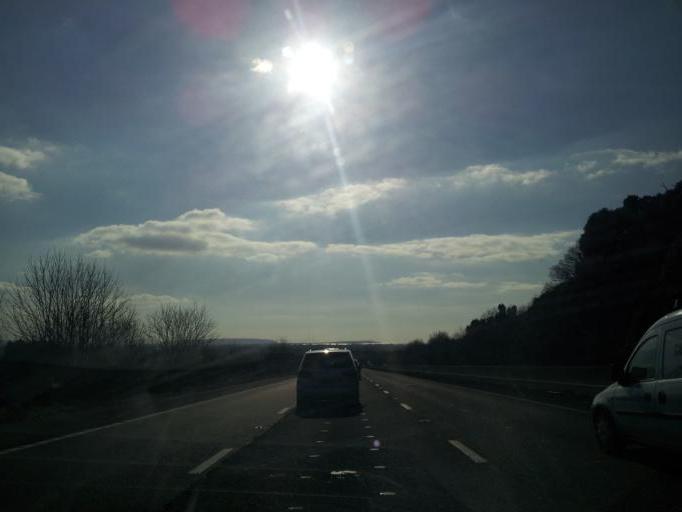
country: GB
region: England
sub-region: North Somerset
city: Clevedon
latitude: 51.4436
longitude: -2.8185
